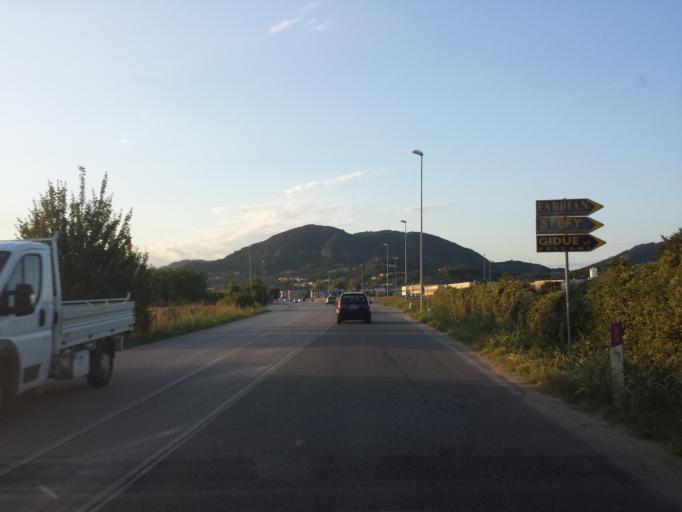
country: IT
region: Veneto
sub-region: Provincia di Vicenza
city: Castelgomberto
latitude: 45.5884
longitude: 11.3788
